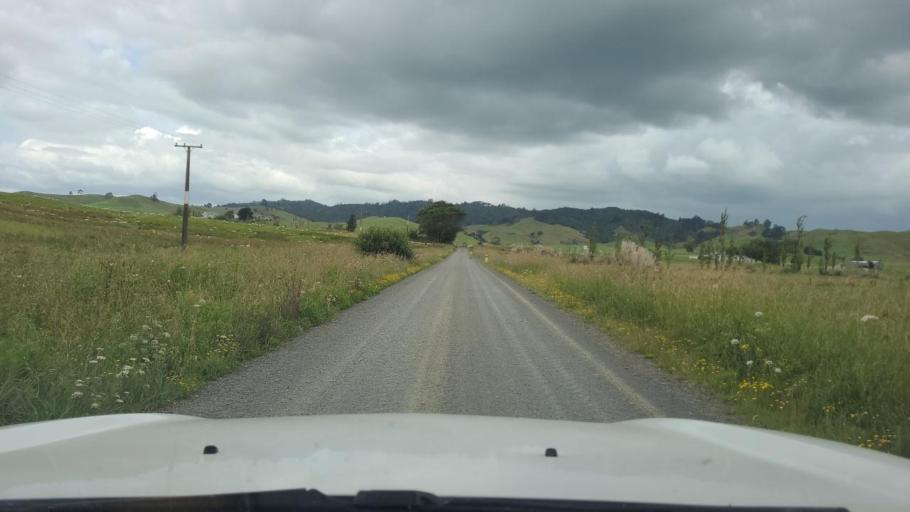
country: NZ
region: Waikato
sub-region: Hamilton City
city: Hamilton
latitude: -37.5705
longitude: 175.4170
